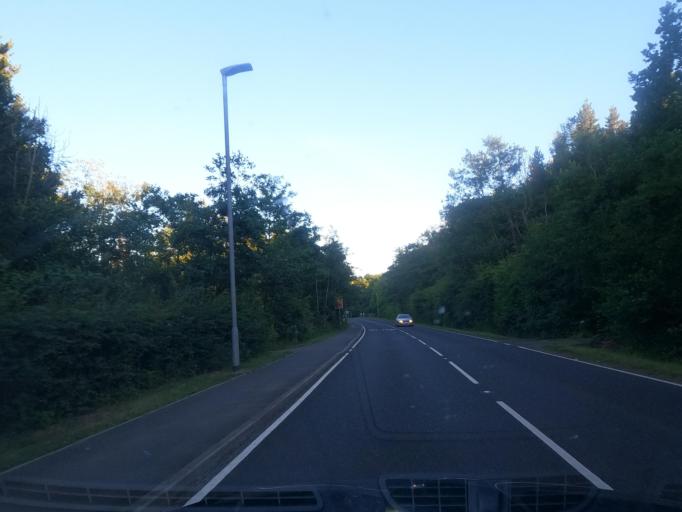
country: GB
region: England
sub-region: Northumberland
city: Seghill
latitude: 55.0783
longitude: -1.5481
